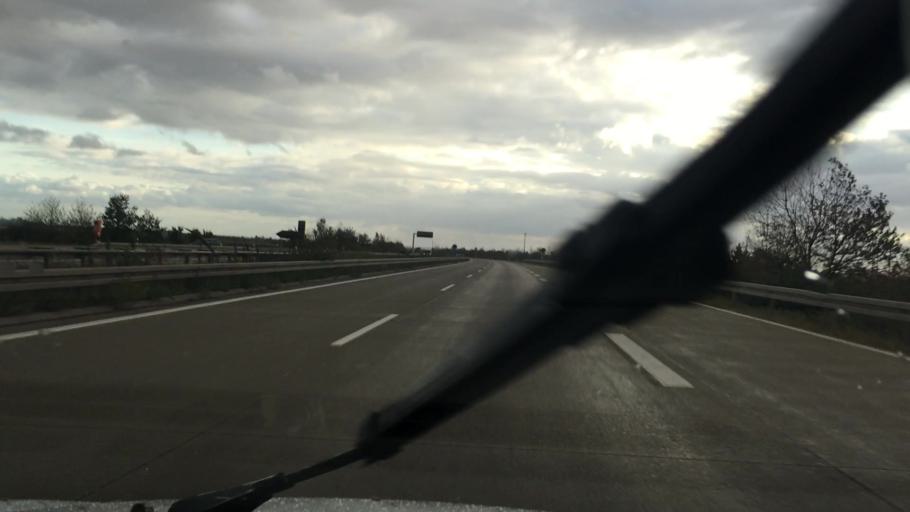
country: DE
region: Saxony-Anhalt
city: Glothe
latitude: 51.8958
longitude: 11.6896
